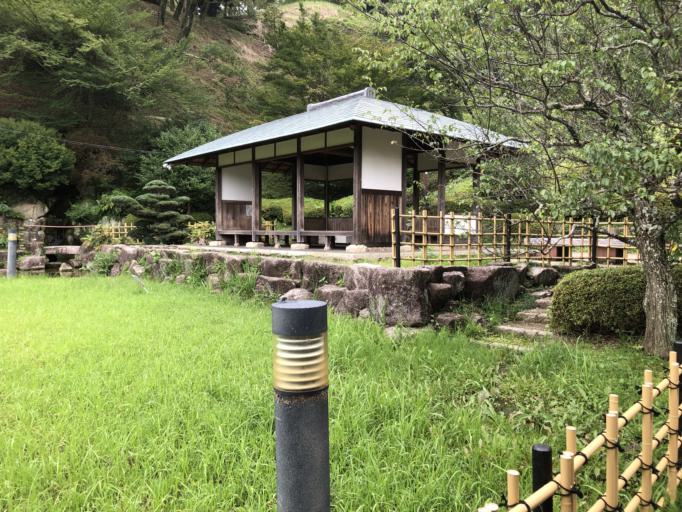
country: JP
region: Shizuoka
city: Fujieda
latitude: 34.8752
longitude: 138.2557
